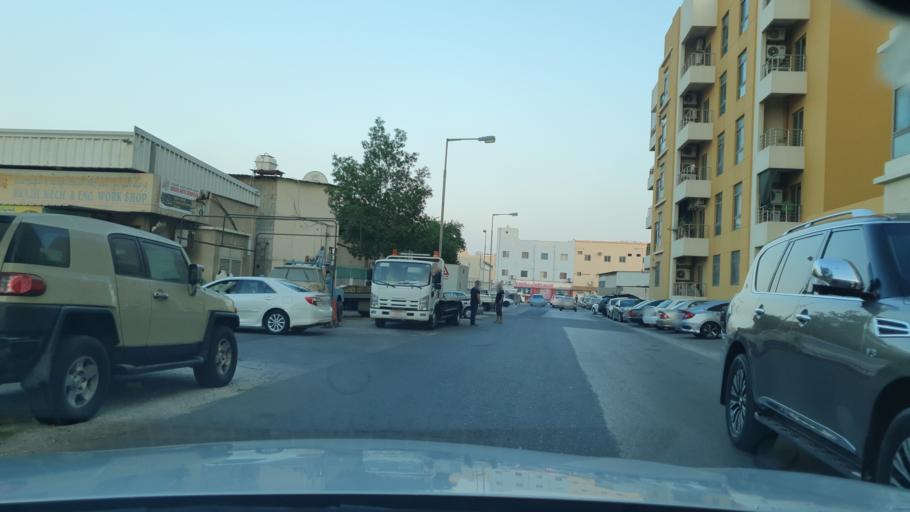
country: BH
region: Northern
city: Madinat `Isa
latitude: 26.1708
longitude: 50.5514
